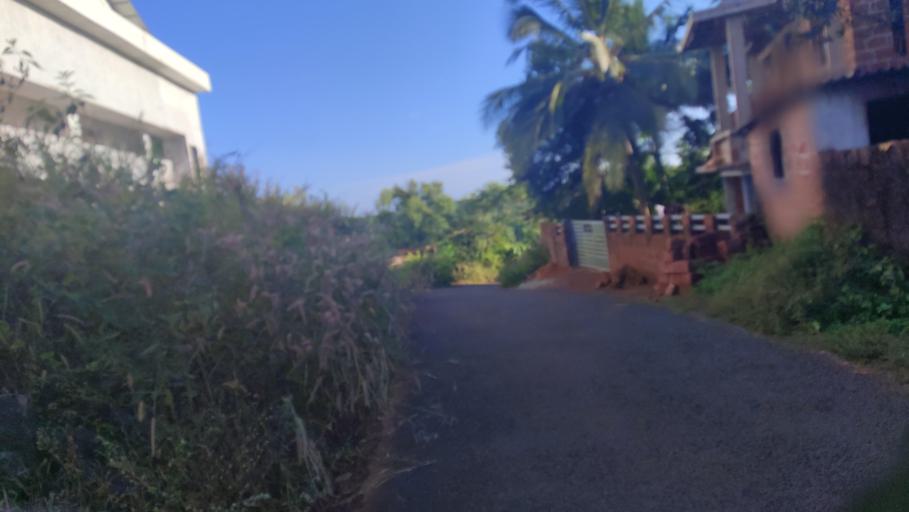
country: IN
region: Kerala
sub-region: Kasaragod District
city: Kasaragod
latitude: 12.5046
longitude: 75.0774
